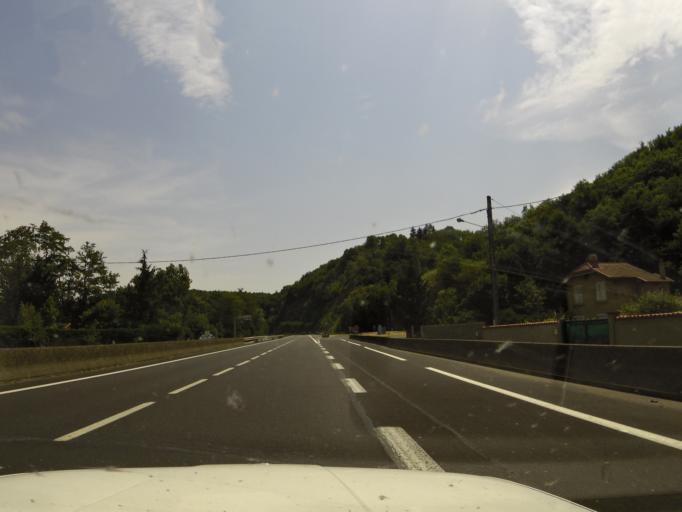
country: FR
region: Auvergne
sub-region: Departement du Puy-de-Dome
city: Issoire
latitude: 45.5800
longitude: 3.2395
